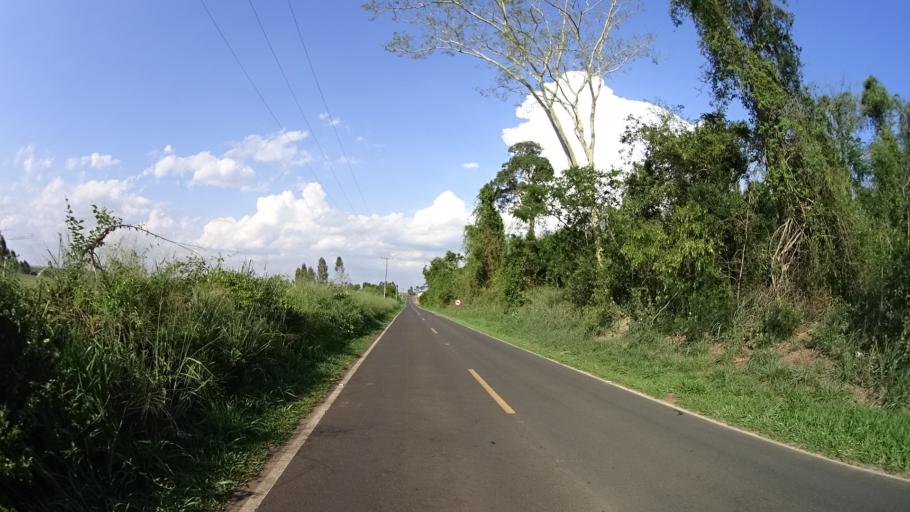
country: BR
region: Sao Paulo
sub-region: Urupes
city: Urupes
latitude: -21.3733
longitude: -49.4758
